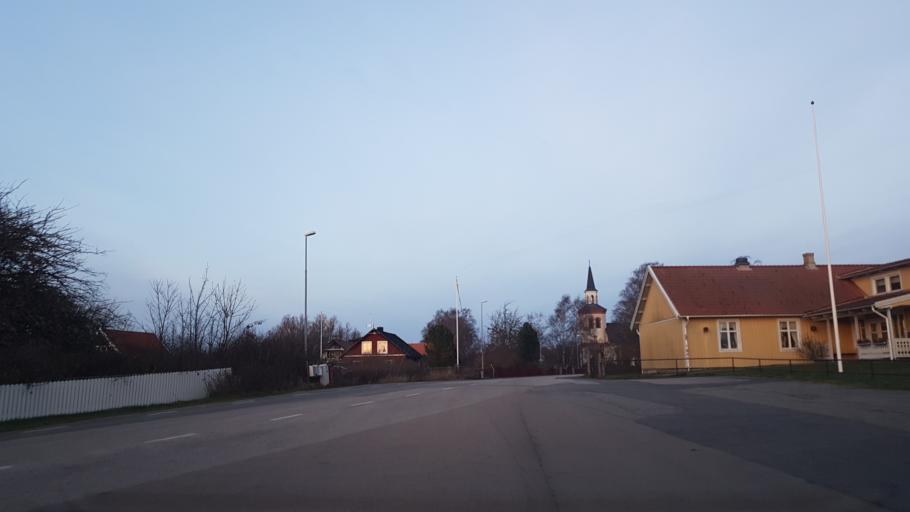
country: SE
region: Blekinge
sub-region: Karlskrona Kommun
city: Jaemjoe
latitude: 56.0934
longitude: 15.8316
